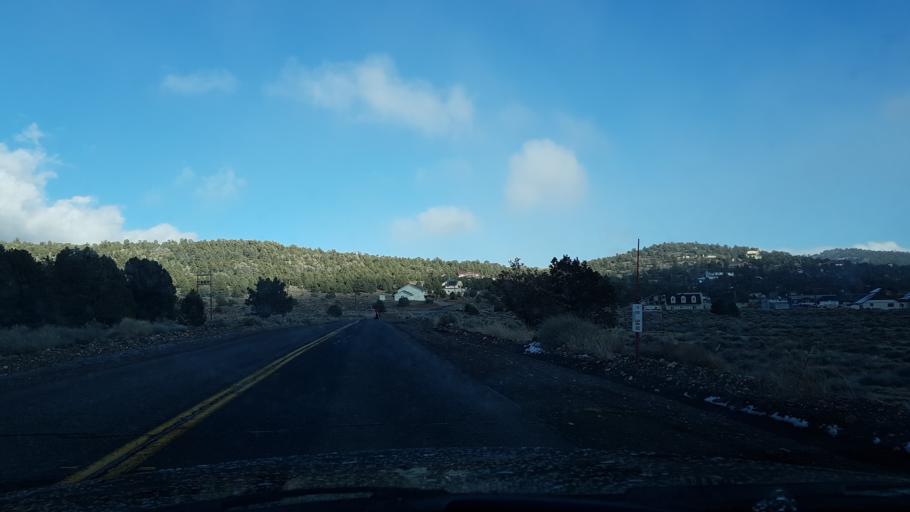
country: US
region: California
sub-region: San Bernardino County
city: Big Bear City
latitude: 34.2933
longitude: -116.8170
